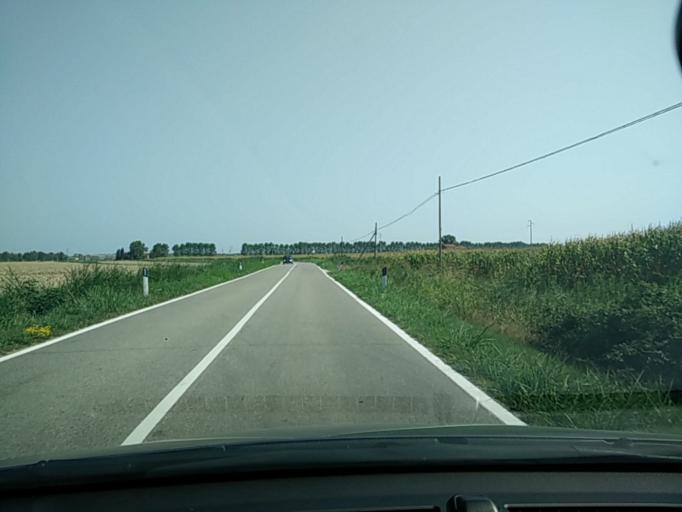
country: IT
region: Veneto
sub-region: Provincia di Venezia
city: La Salute di Livenza
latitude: 45.6269
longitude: 12.8386
